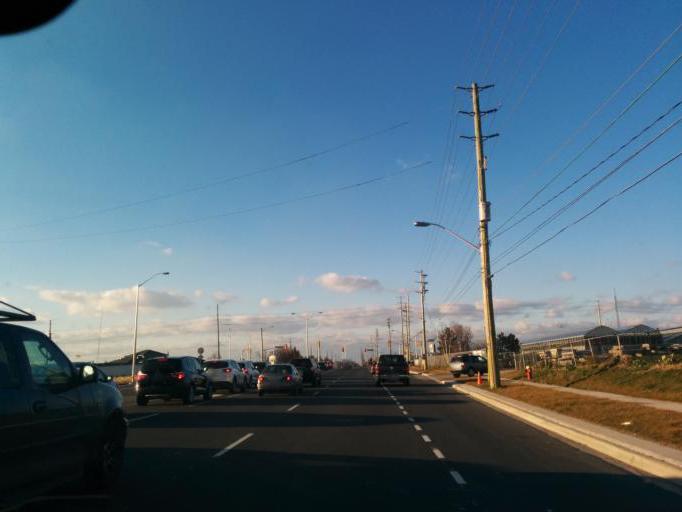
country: CA
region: Ontario
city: Oakville
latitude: 43.5071
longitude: -79.6956
